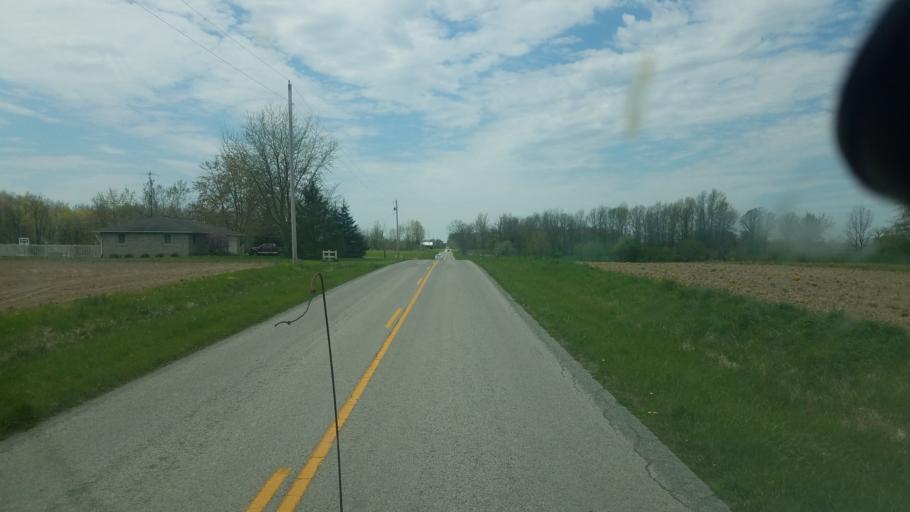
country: US
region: Ohio
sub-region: Hardin County
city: Ada
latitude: 40.7940
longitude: -83.9115
